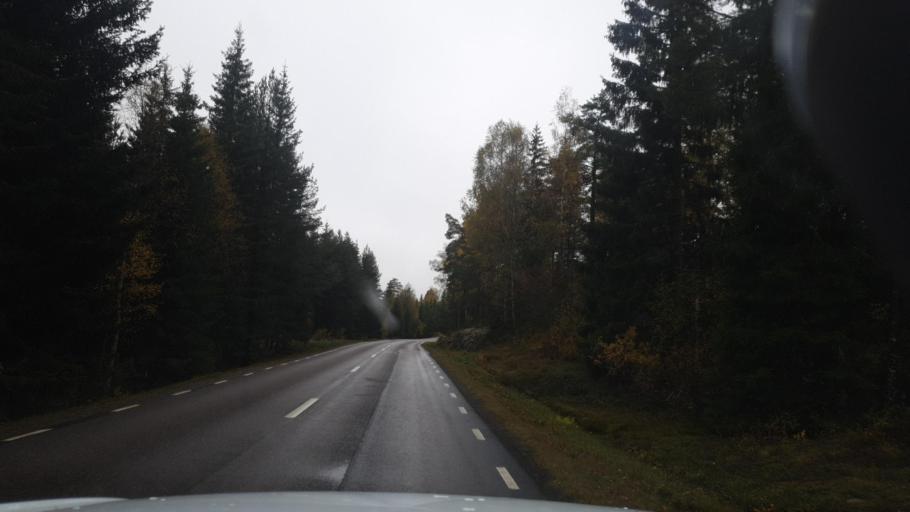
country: SE
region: Vaermland
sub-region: Eda Kommun
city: Amotfors
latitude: 59.6302
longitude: 12.3439
